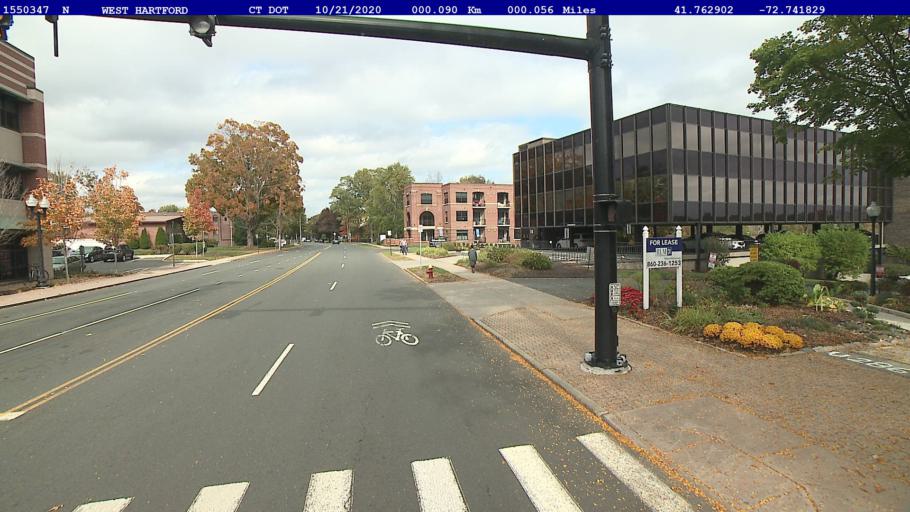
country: US
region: Connecticut
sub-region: Hartford County
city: West Hartford
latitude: 41.7629
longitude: -72.7418
